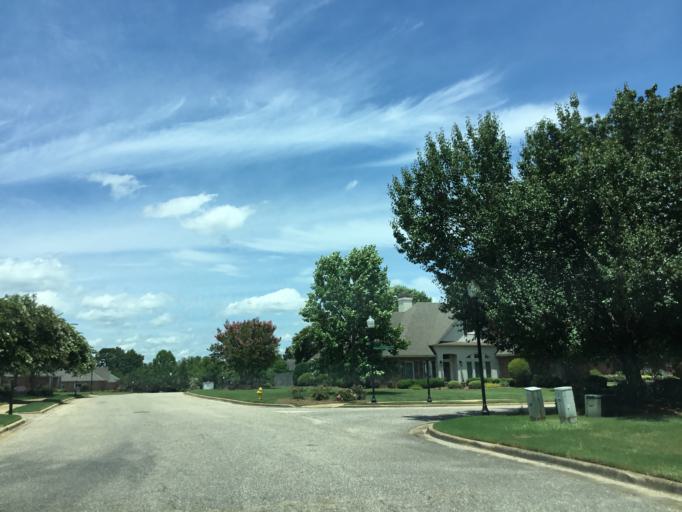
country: US
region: Alabama
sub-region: Montgomery County
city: Pike Road
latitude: 32.3756
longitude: -86.1354
